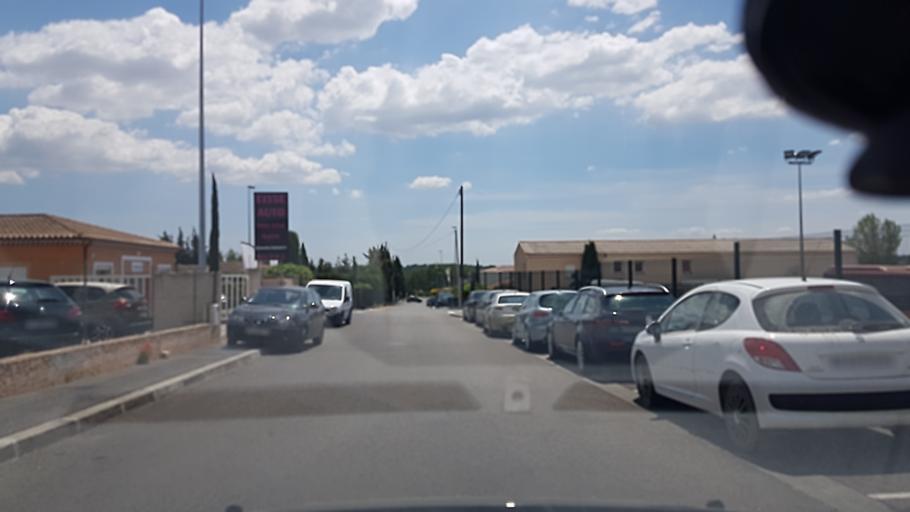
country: FR
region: Provence-Alpes-Cote d'Azur
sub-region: Departement des Bouches-du-Rhone
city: Eguilles
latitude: 43.5468
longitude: 5.3627
